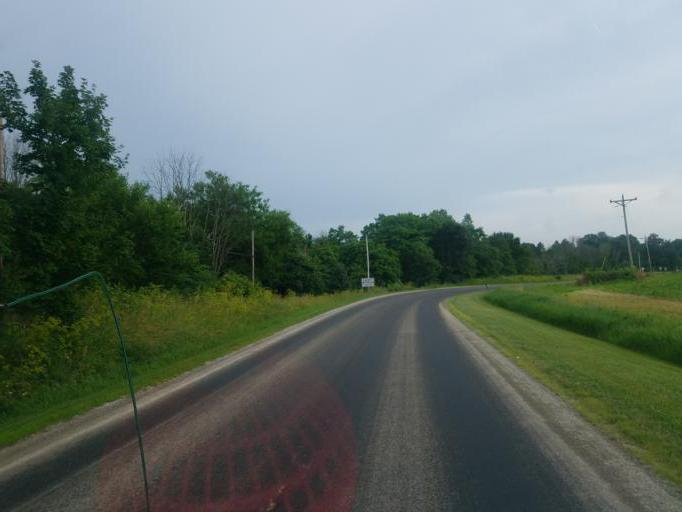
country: US
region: Ohio
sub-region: Ashland County
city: Ashland
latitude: 40.7873
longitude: -82.2177
